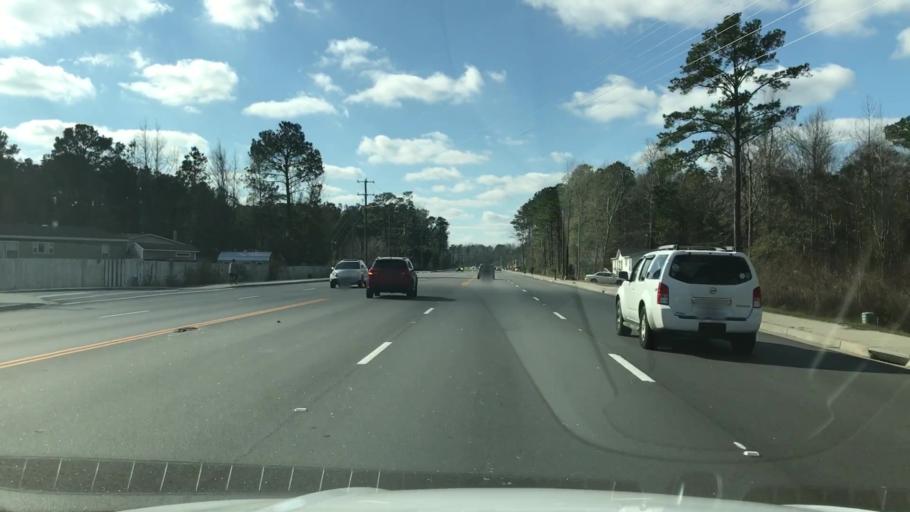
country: US
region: South Carolina
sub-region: Horry County
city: Socastee
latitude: 33.6440
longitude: -79.0276
